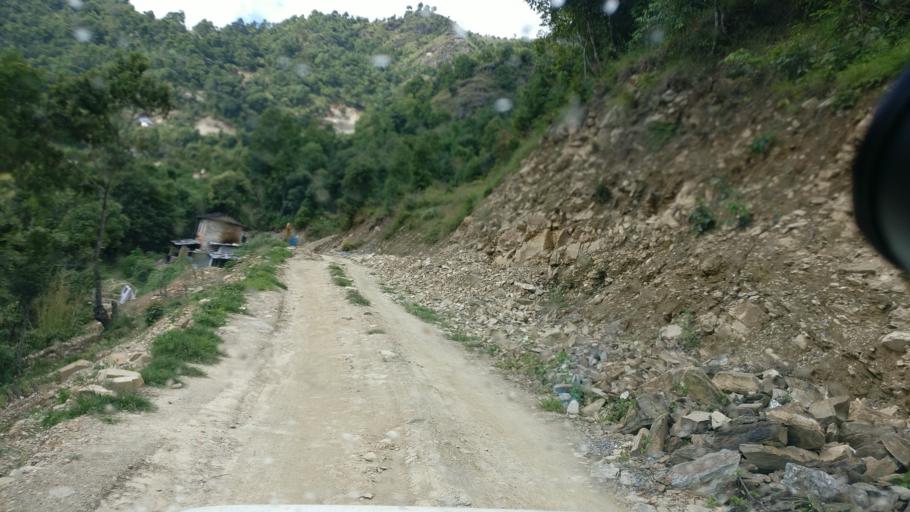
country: NP
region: Western Region
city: Baglung
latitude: 28.2722
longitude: 83.6451
